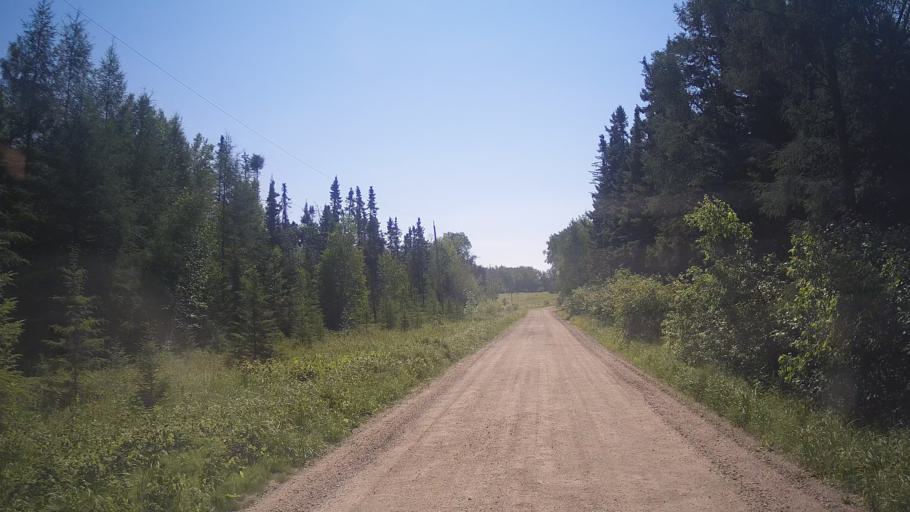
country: CA
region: Ontario
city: Dryden
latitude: 49.8186
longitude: -93.3342
